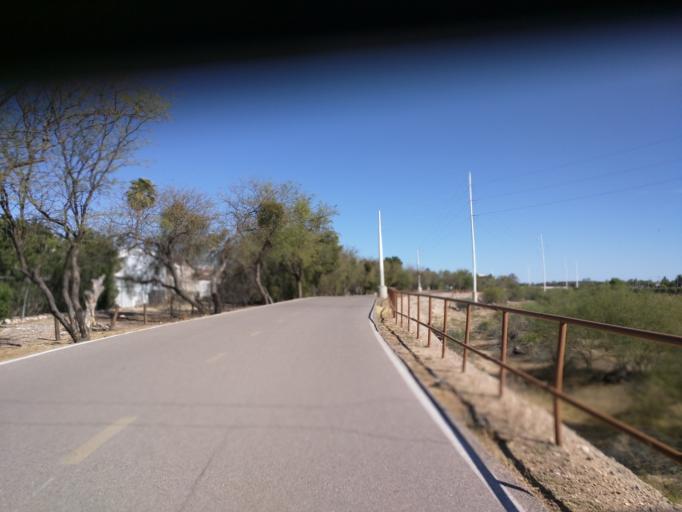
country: US
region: Arizona
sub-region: Pima County
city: Flowing Wells
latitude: 32.2945
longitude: -110.9772
